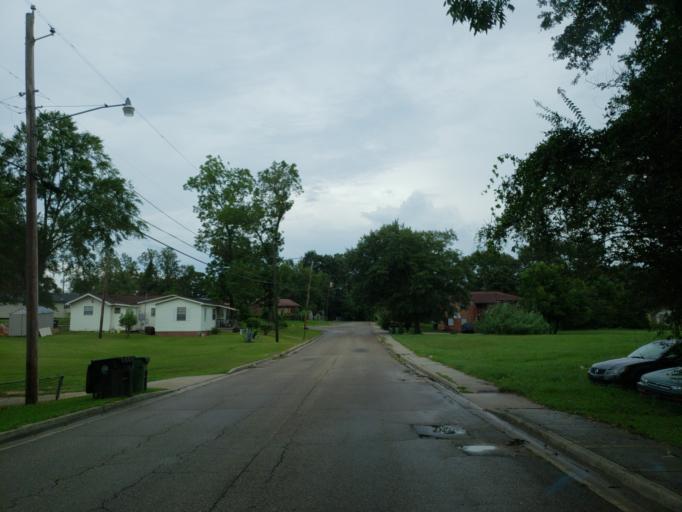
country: US
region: Mississippi
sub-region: Forrest County
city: Hattiesburg
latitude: 31.3126
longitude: -89.2994
